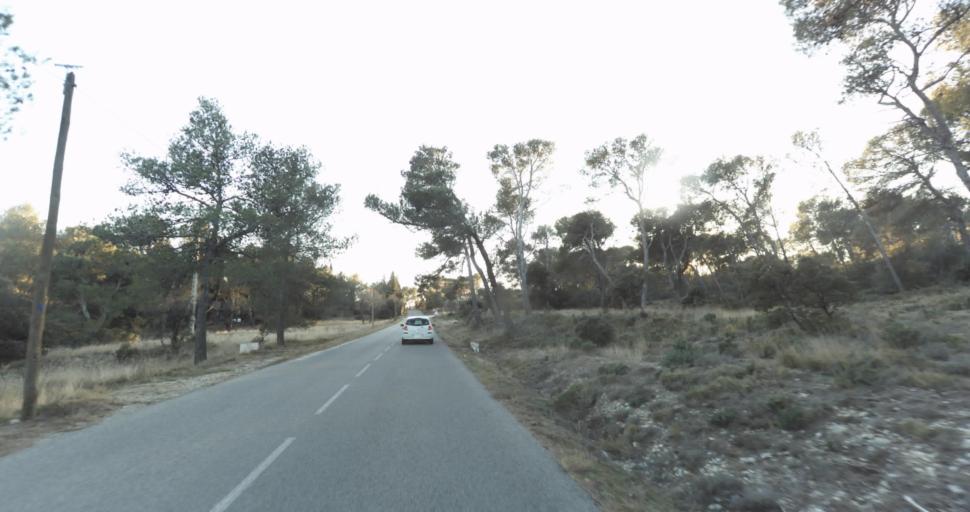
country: FR
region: Provence-Alpes-Cote d'Azur
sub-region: Departement des Bouches-du-Rhone
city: Barbentane
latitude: 43.8746
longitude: 4.7314
